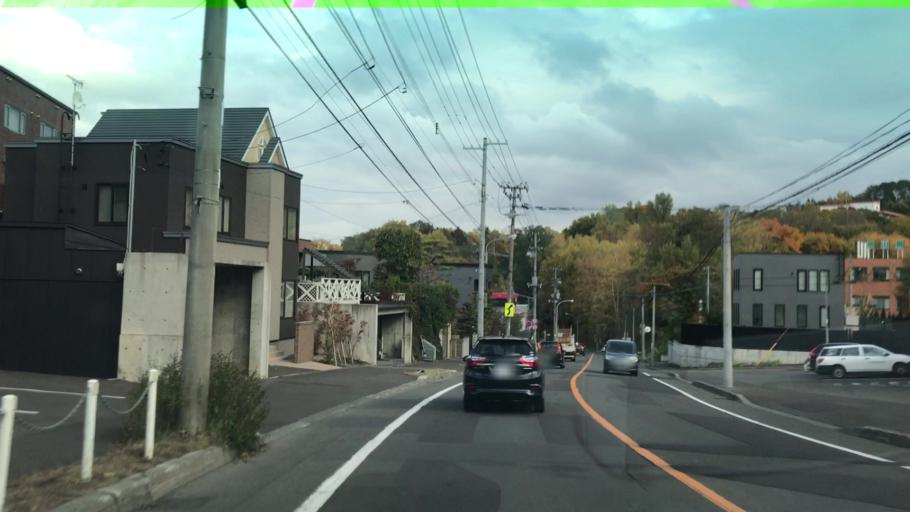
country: JP
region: Hokkaido
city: Sapporo
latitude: 43.0434
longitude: 141.3105
